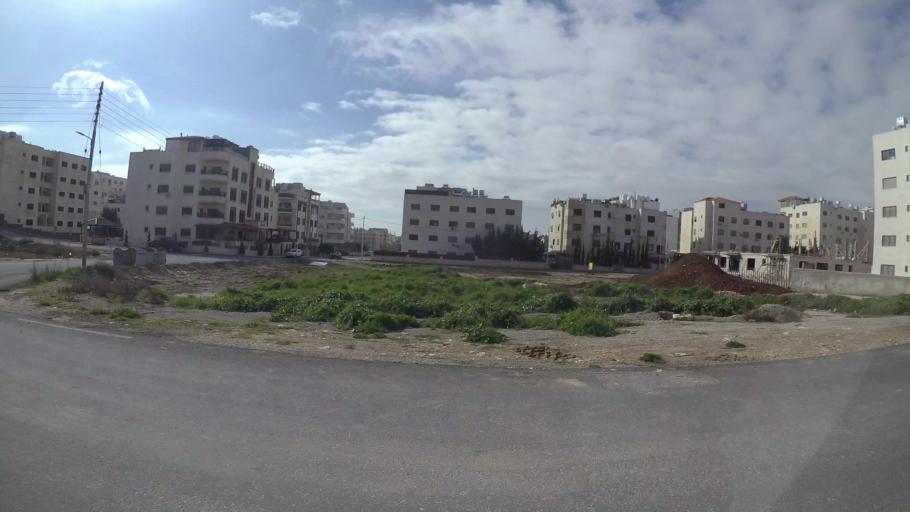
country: JO
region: Amman
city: Al Jubayhah
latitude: 32.0035
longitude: 35.8465
